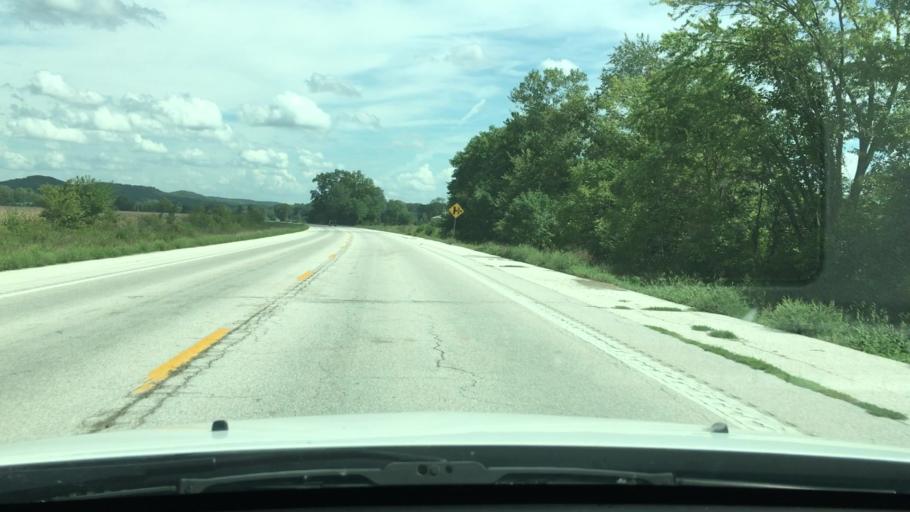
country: US
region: Missouri
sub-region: Pike County
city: Bowling Green
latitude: 39.3841
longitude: -91.1275
